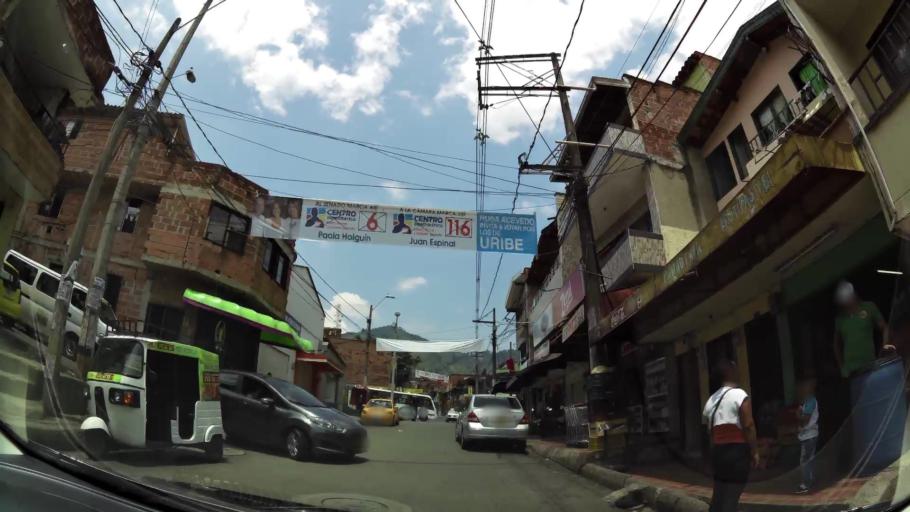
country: CO
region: Antioquia
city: Itagui
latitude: 6.1791
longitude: -75.6093
